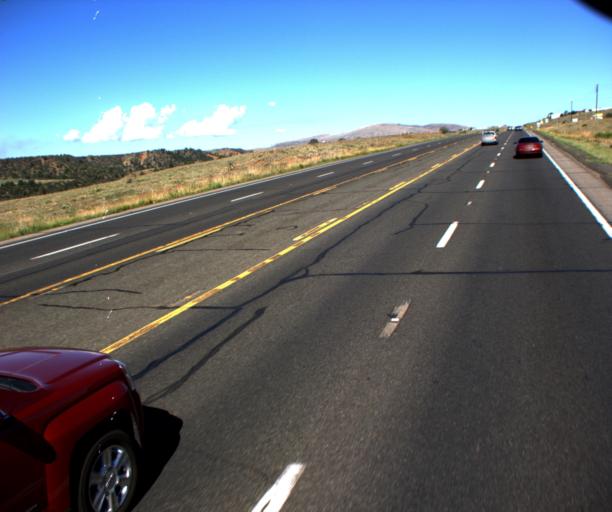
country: US
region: Arizona
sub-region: Yavapai County
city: Prescott Valley
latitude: 34.5753
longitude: -112.2850
